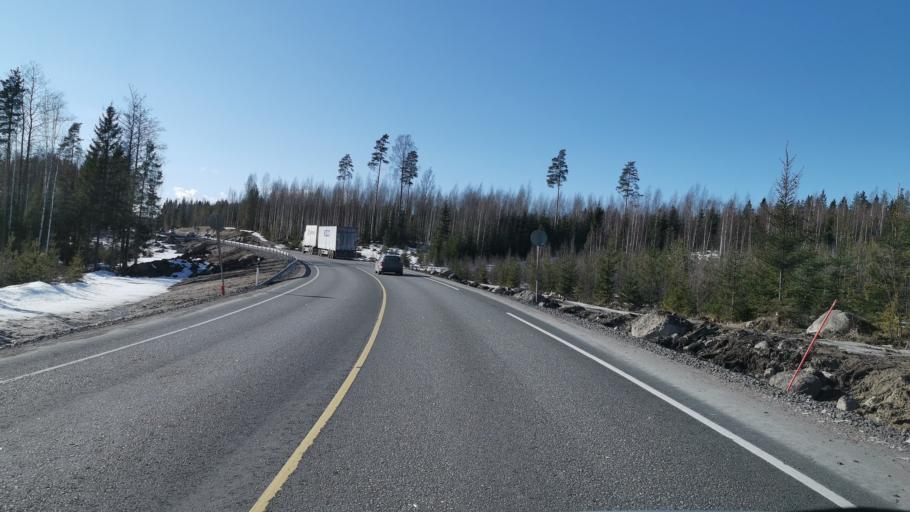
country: FI
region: Kymenlaakso
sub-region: Kouvola
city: Kouvola
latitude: 60.8693
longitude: 26.5495
